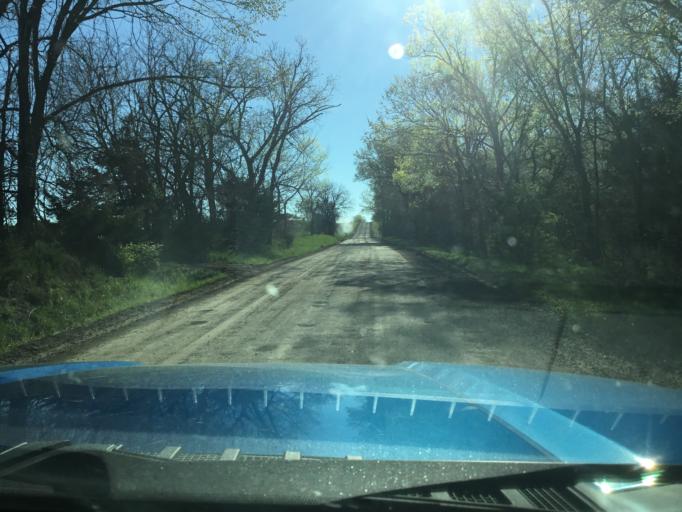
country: US
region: Kansas
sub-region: Douglas County
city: Lawrence
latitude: 38.9568
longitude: -95.3608
